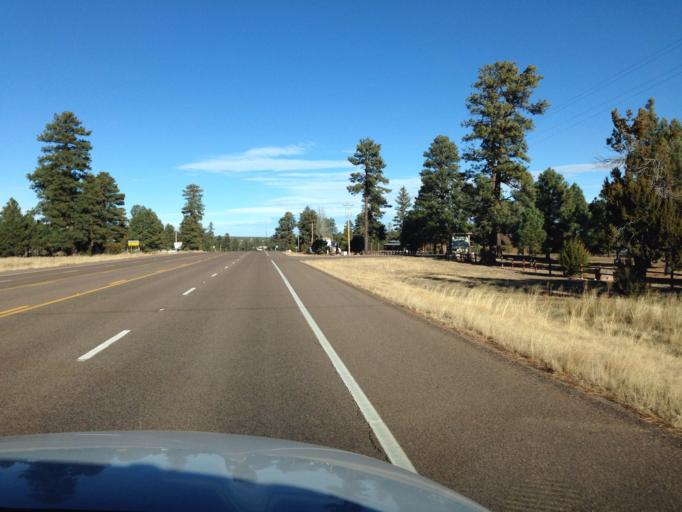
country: US
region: Arizona
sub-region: Navajo County
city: Heber-Overgaard
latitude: 34.4121
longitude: -110.5708
